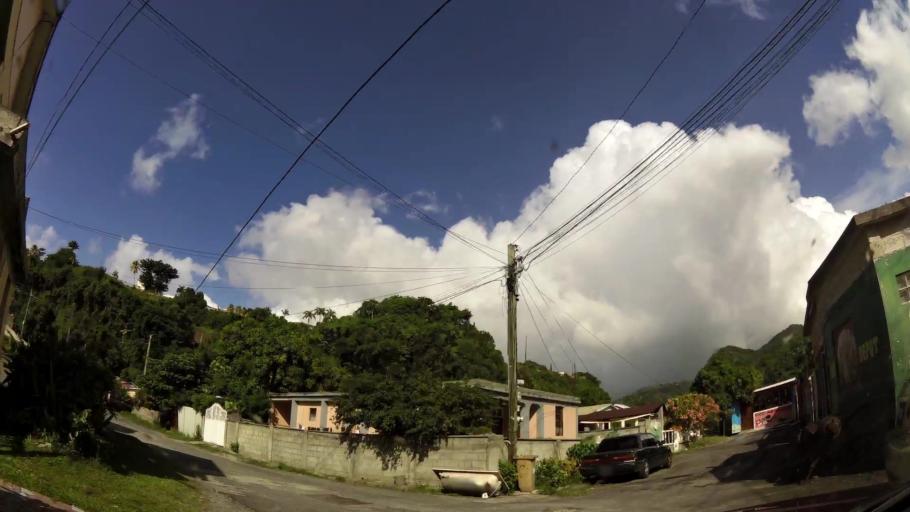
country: DM
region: Saint George
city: Roseau
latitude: 15.3026
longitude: -61.3767
